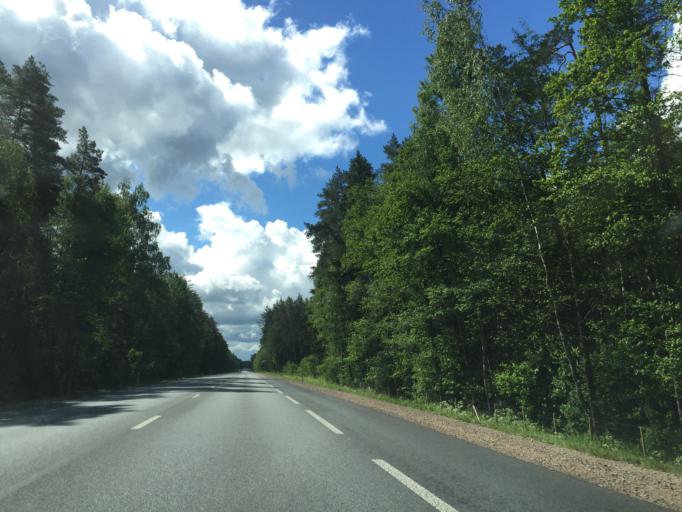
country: LV
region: Kekava
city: Kekava
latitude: 56.7483
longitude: 24.2496
